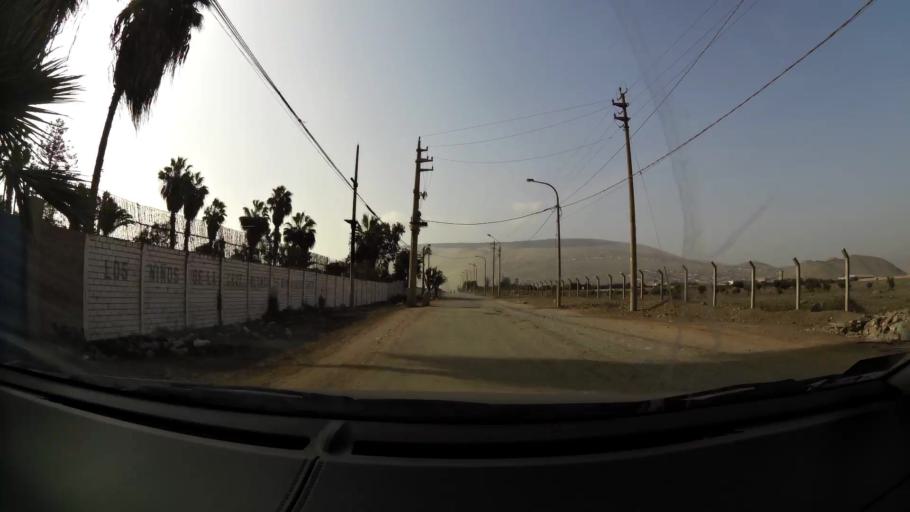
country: PE
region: Lima
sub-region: Lima
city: Santa Rosa
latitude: -11.7555
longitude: -77.1694
